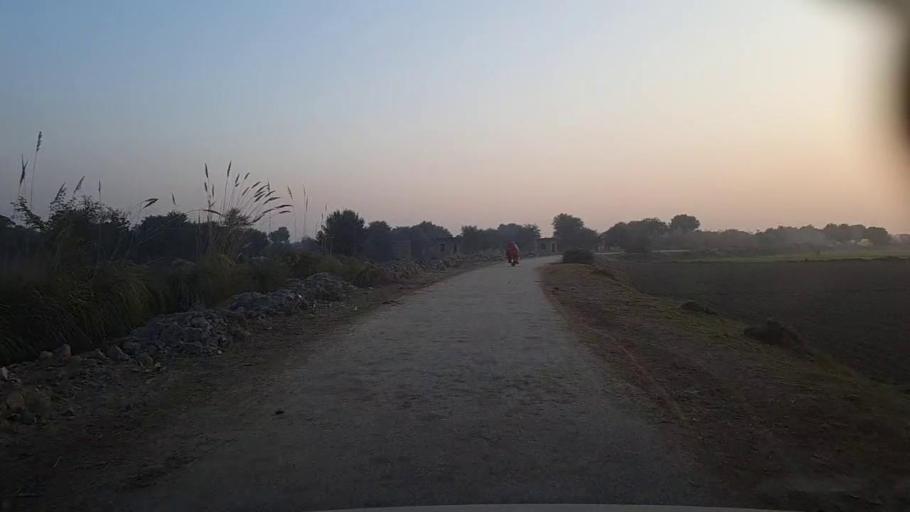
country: PK
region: Sindh
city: Karaundi
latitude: 26.8366
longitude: 68.3692
